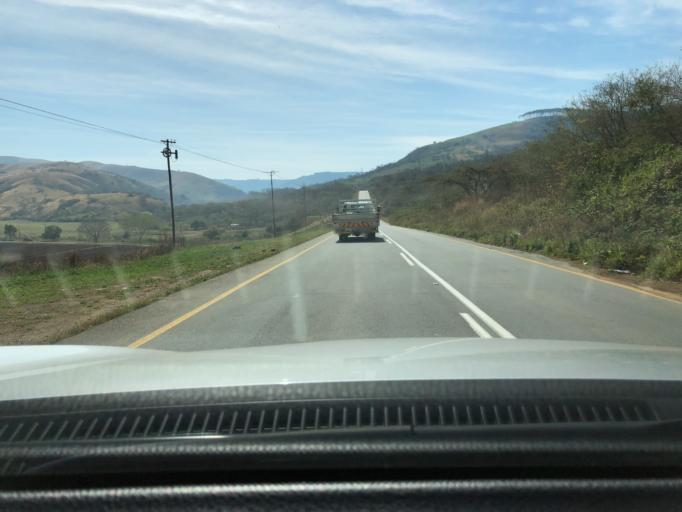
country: ZA
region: KwaZulu-Natal
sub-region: uMgungundlovu District Municipality
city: Richmond
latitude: -29.9548
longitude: 30.2556
